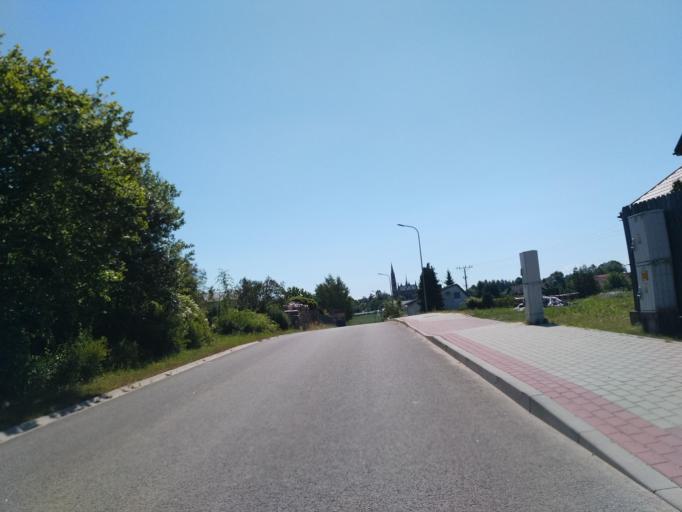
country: PL
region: Subcarpathian Voivodeship
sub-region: Powiat krosnienski
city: Korczyna
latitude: 49.7192
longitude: 21.8013
